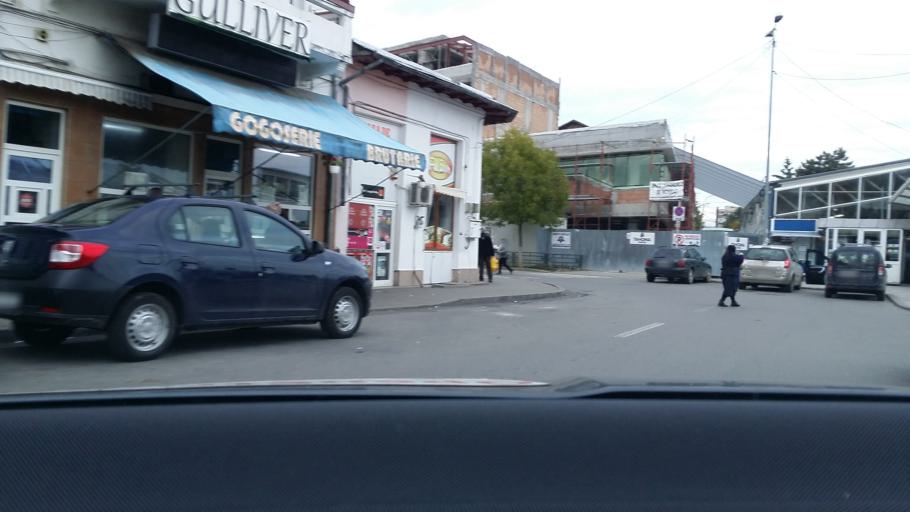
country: RO
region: Prahova
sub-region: Municipiul Campina
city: Campina
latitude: 45.1247
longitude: 25.7356
